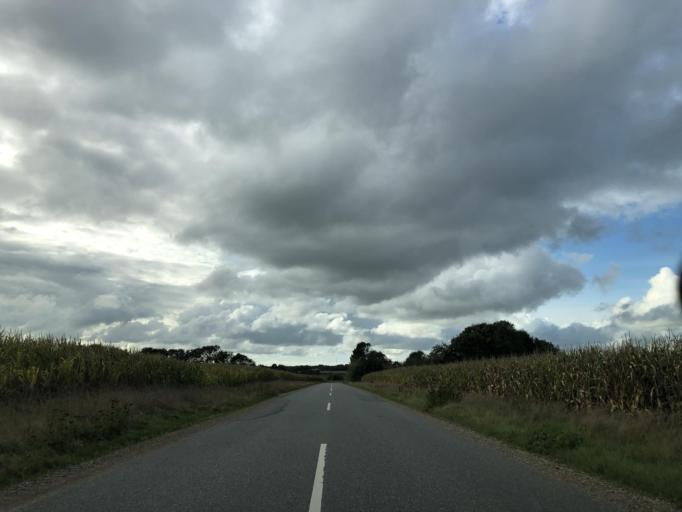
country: DK
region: South Denmark
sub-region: Varde Kommune
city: Olgod
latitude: 55.7554
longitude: 8.6469
